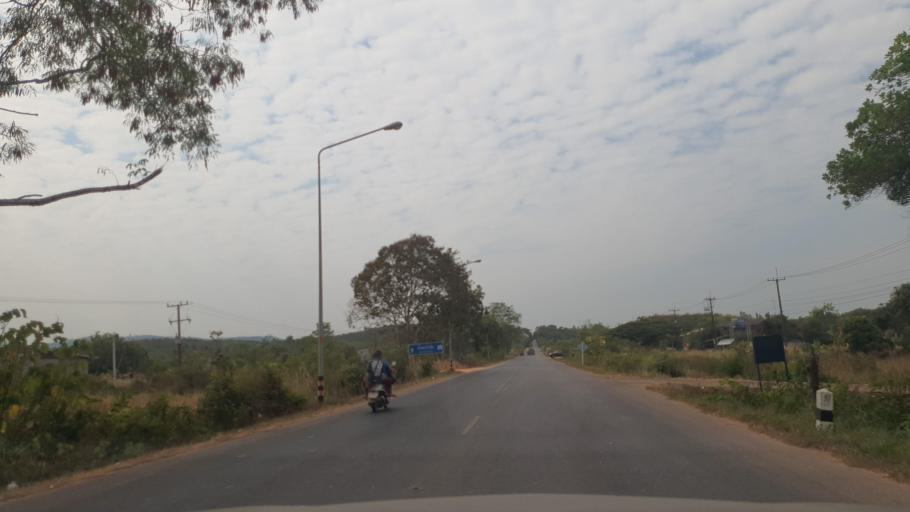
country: TH
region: Changwat Bueng Kan
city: Bung Khla
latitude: 18.3053
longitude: 103.9667
